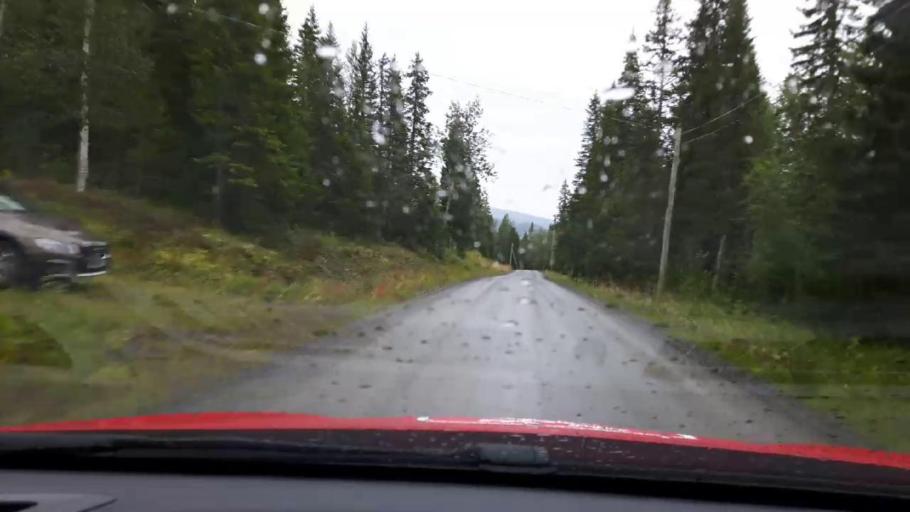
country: SE
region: Jaemtland
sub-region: Are Kommun
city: Are
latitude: 63.5076
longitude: 12.7276
